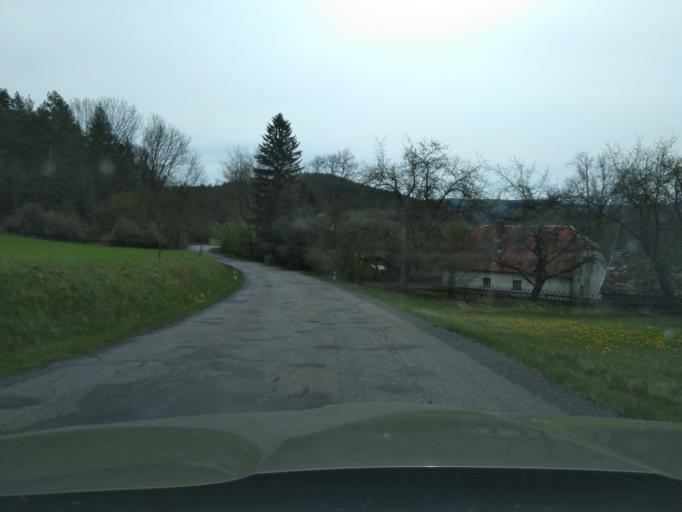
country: CZ
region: Plzensky
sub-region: Okres Klatovy
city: Kasperske Hory
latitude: 49.1941
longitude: 13.6208
